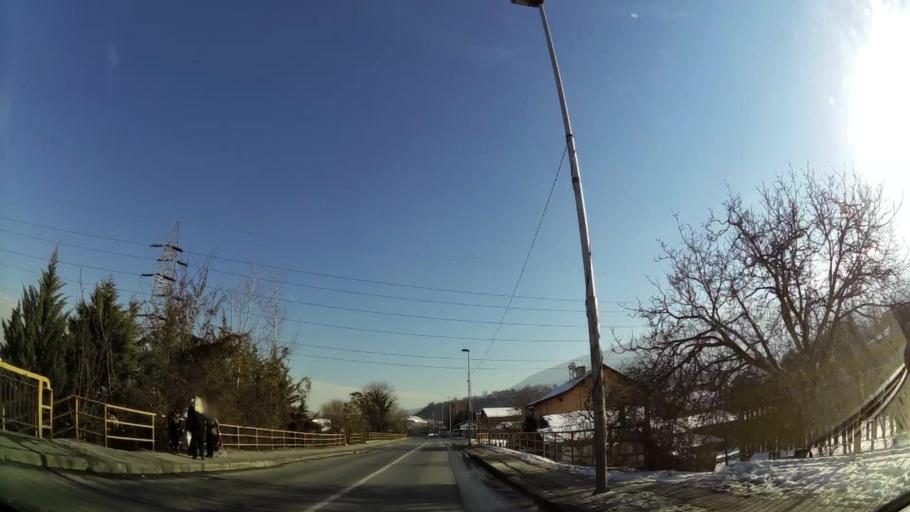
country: MK
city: Krushopek
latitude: 42.0012
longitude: 21.3776
